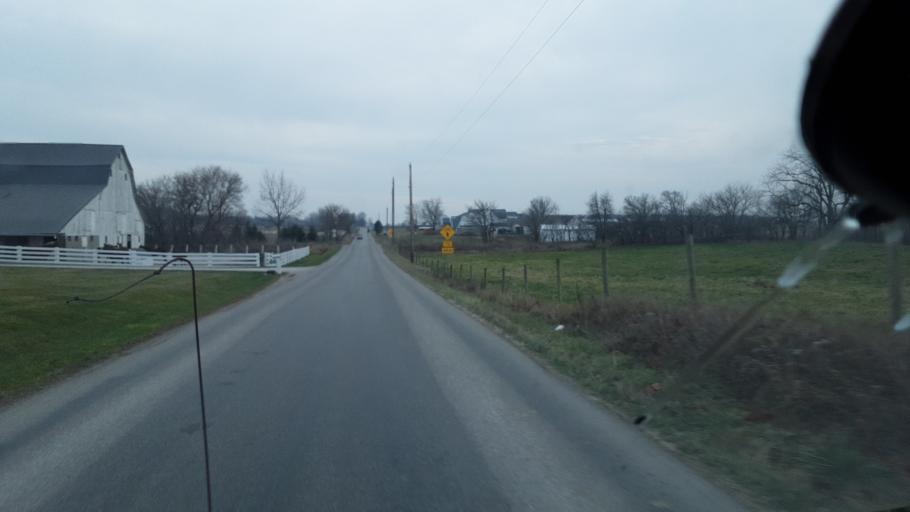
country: US
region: Indiana
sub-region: Elkhart County
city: Middlebury
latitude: 41.6812
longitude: -85.6197
